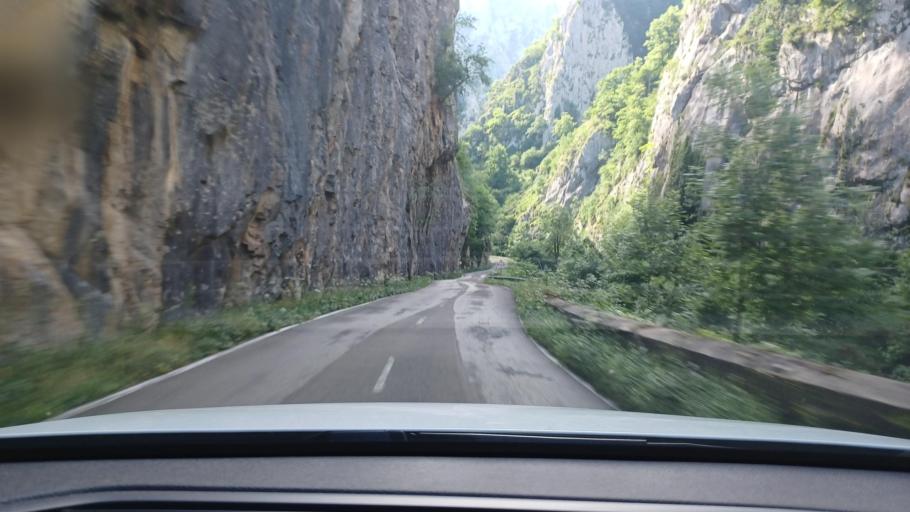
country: ES
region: Asturias
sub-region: Province of Asturias
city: La Plaza
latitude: 43.1232
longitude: -6.0565
